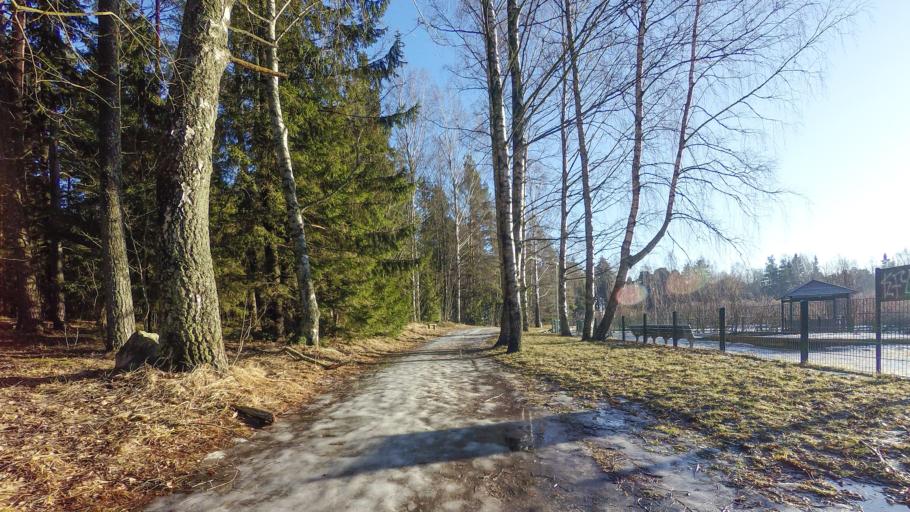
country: FI
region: Uusimaa
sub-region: Helsinki
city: Vantaa
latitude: 60.1777
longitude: 25.0605
